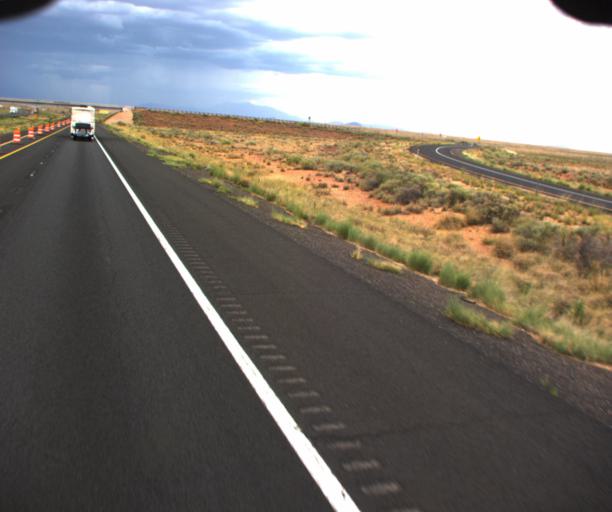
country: US
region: Arizona
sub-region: Coconino County
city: LeChee
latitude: 35.1172
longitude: -111.0875
